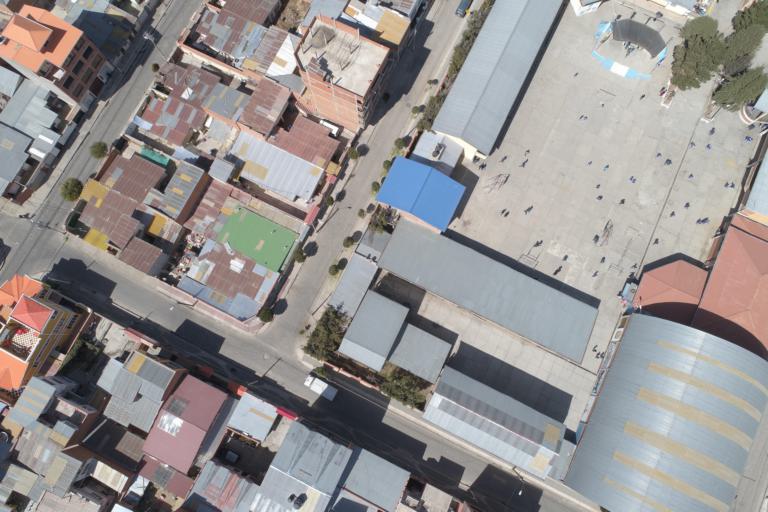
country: BO
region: La Paz
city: La Paz
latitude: -16.5259
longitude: -68.1555
